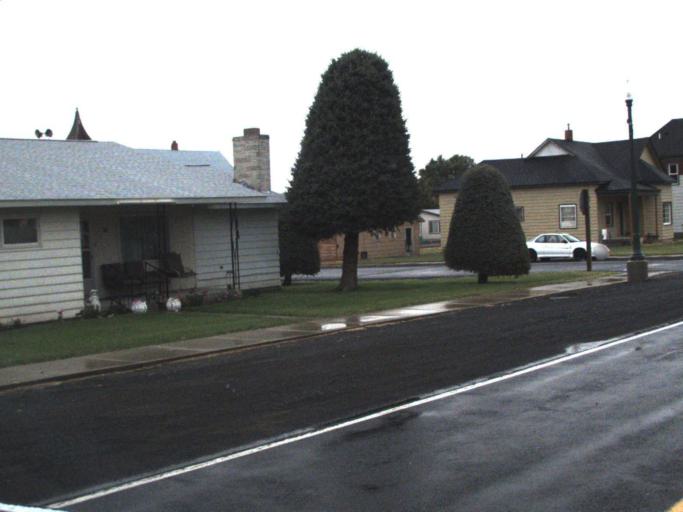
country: US
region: Washington
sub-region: Lincoln County
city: Davenport
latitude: 47.4825
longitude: -118.2546
